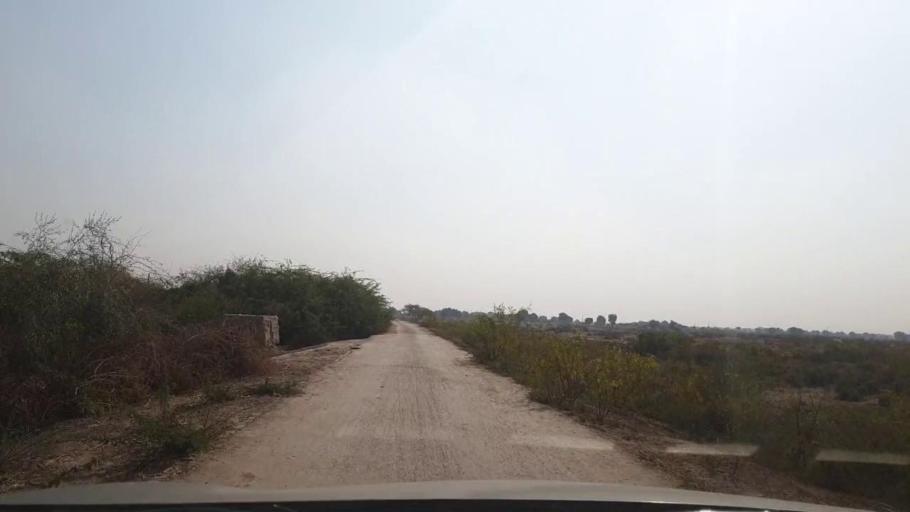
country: PK
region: Sindh
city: Tando Allahyar
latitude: 25.5728
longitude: 68.8181
